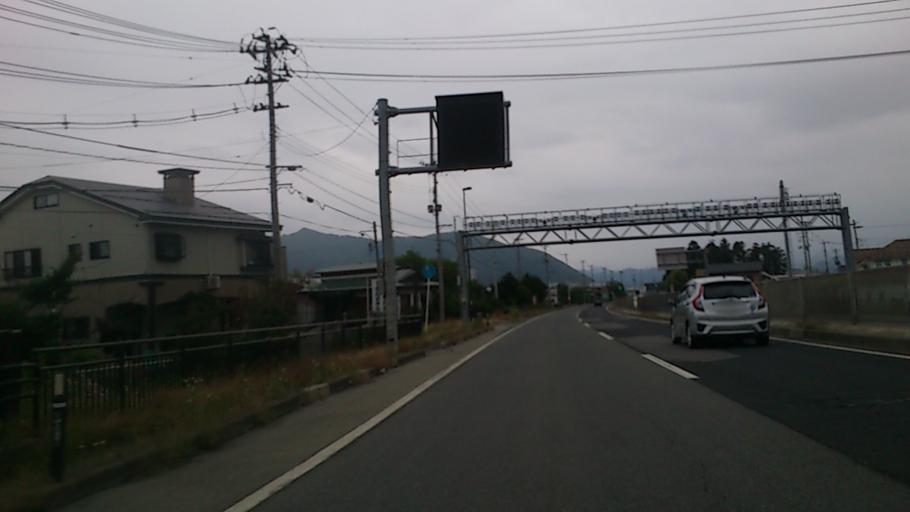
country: JP
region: Yamagata
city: Tendo
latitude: 38.3912
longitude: 140.3802
